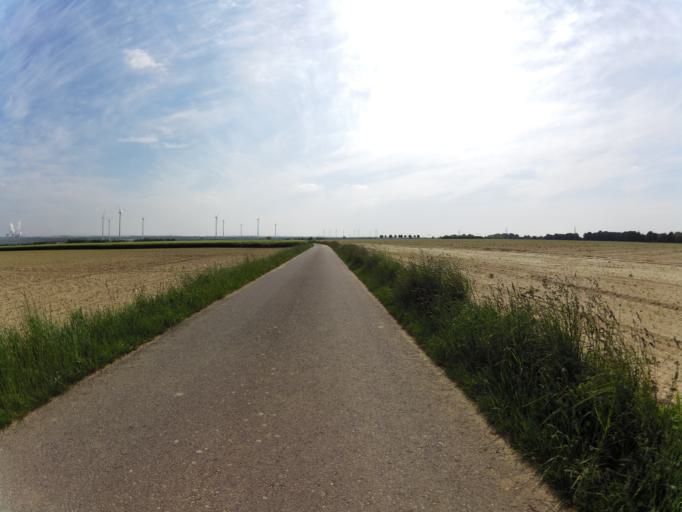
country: DE
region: North Rhine-Westphalia
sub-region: Regierungsbezirk Koln
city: Aldenhoven
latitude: 50.8974
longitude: 6.3089
